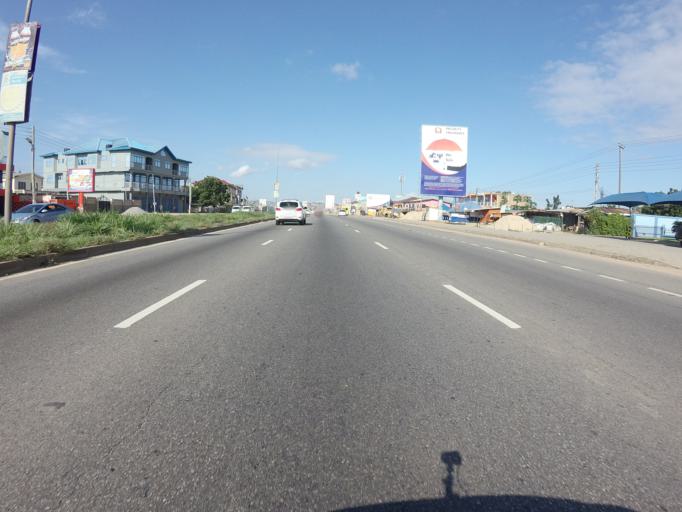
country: GH
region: Greater Accra
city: Gbawe
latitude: 5.5530
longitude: -0.3238
